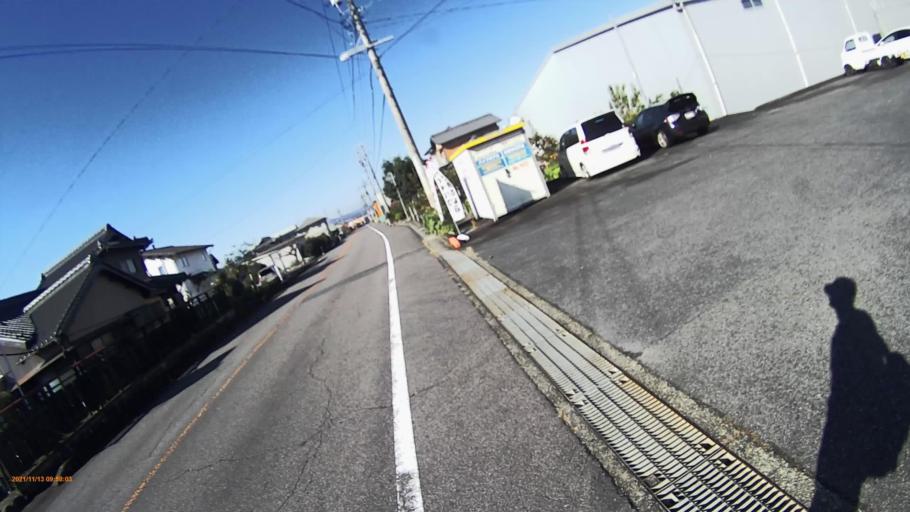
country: JP
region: Gifu
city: Minokamo
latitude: 35.4360
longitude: 137.0511
